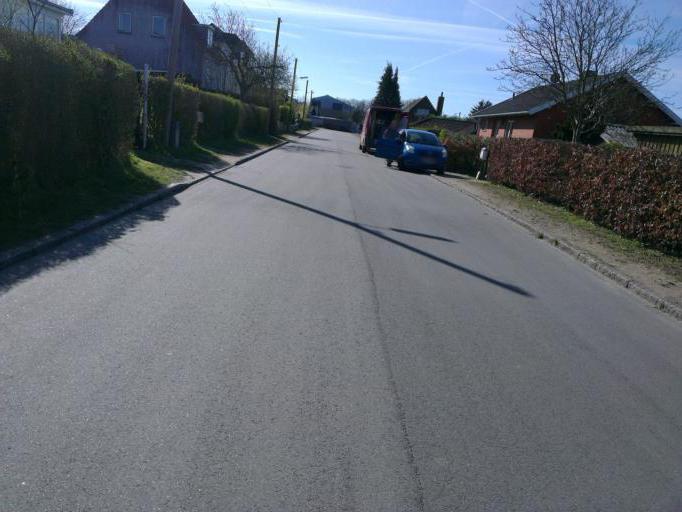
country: DK
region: Capital Region
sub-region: Frederikssund Kommune
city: Frederikssund
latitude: 55.8327
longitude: 12.0703
